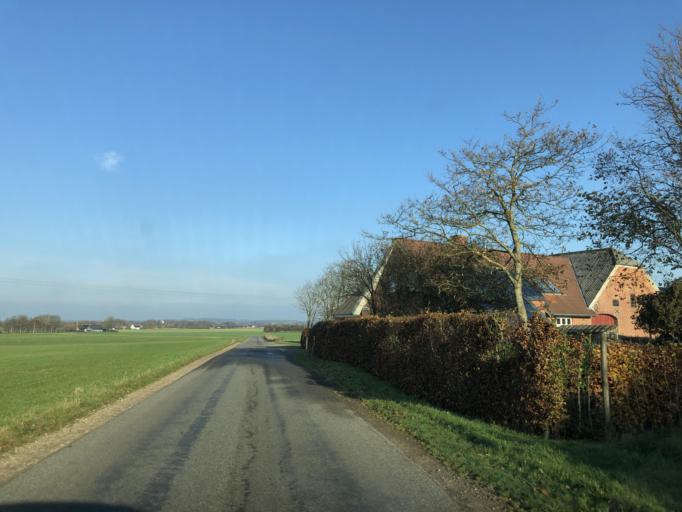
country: DK
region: Central Jutland
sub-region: Holstebro Kommune
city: Vinderup
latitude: 56.3936
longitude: 8.7431
